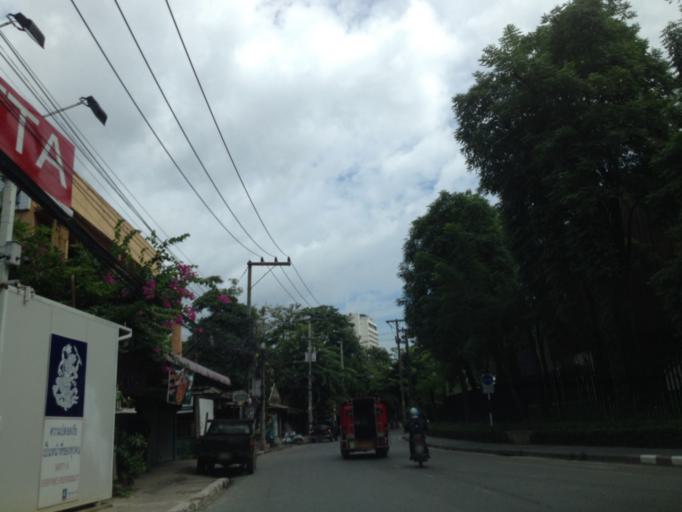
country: TH
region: Chiang Mai
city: Chiang Mai
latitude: 18.7817
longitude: 99.0033
